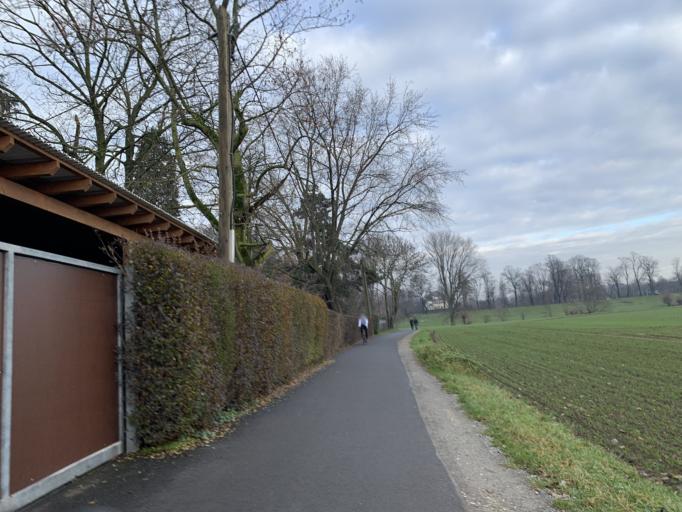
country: DE
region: North Rhine-Westphalia
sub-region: Regierungsbezirk Dusseldorf
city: Meerbusch
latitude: 51.2957
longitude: 6.7303
